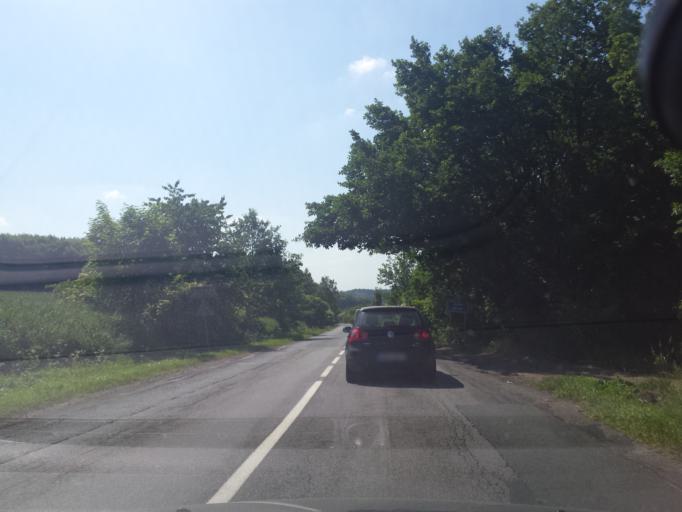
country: CZ
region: Central Bohemia
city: Kralupy nad Vltavou
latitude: 50.2172
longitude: 14.3146
